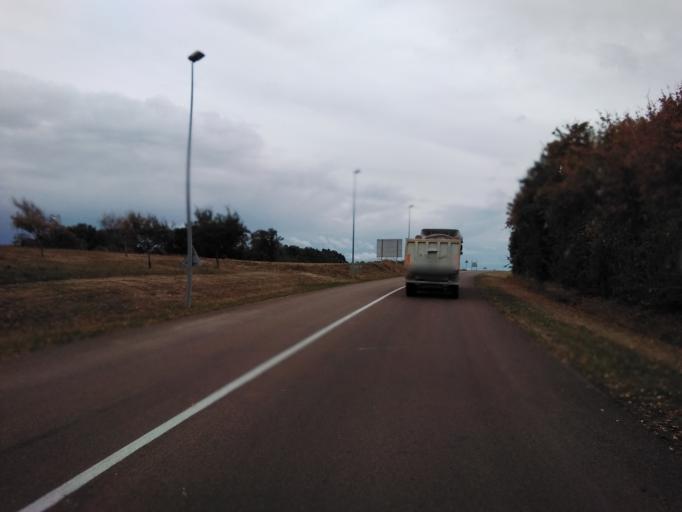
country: FR
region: Champagne-Ardenne
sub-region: Departement de l'Aube
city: Brienne-le-Chateau
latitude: 48.3474
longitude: 4.5283
